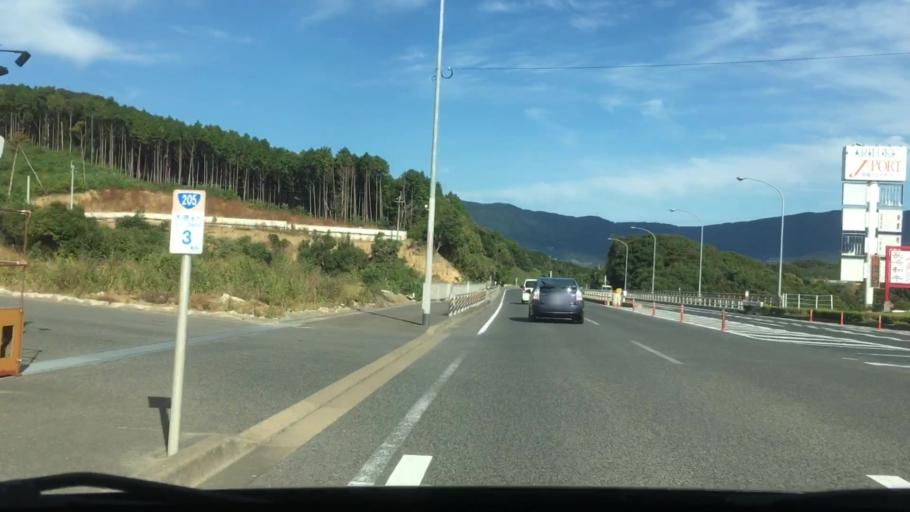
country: JP
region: Nagasaki
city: Sasebo
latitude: 33.1266
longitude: 129.7887
